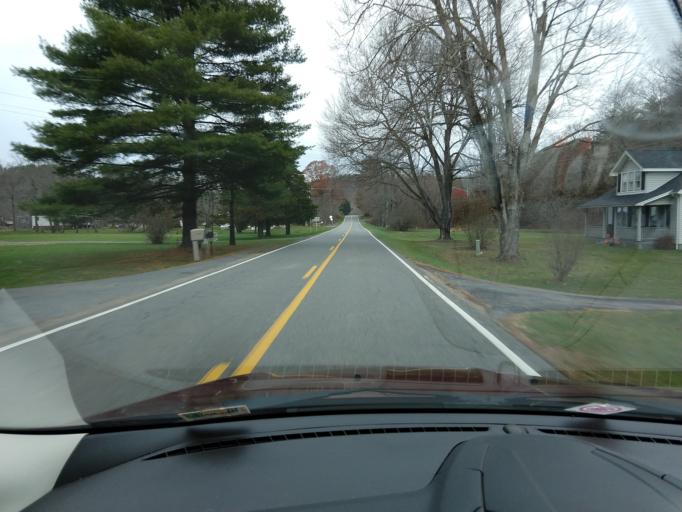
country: US
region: West Virginia
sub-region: Greenbrier County
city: White Sulphur Springs
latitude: 37.7483
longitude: -80.1682
